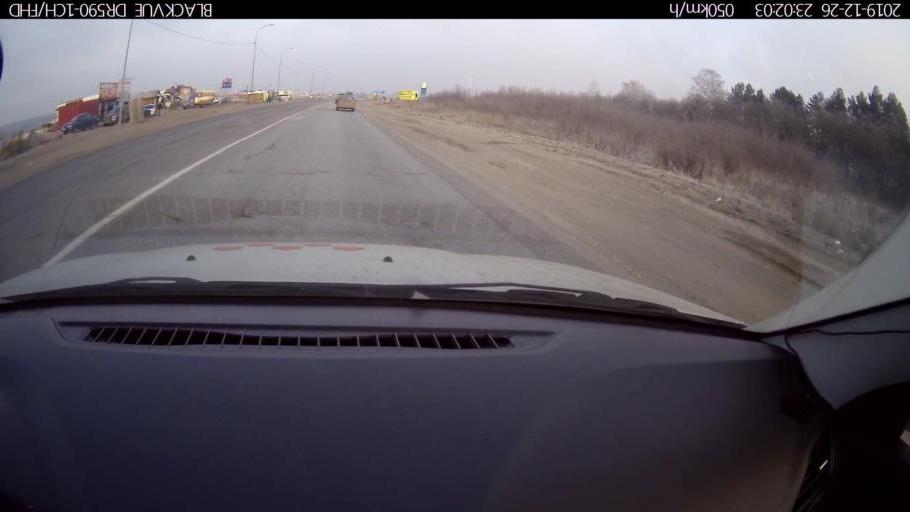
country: RU
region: Nizjnij Novgorod
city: Burevestnik
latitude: 56.1700
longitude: 43.7305
